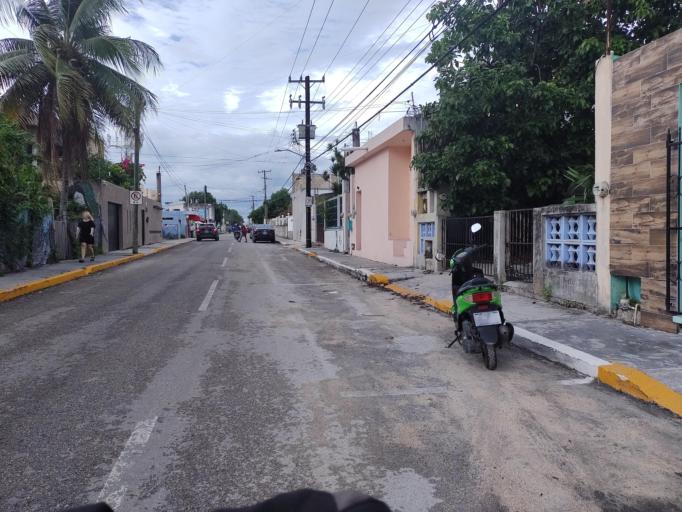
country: MX
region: Quintana Roo
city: San Miguel de Cozumel
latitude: 20.5023
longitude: -86.9524
